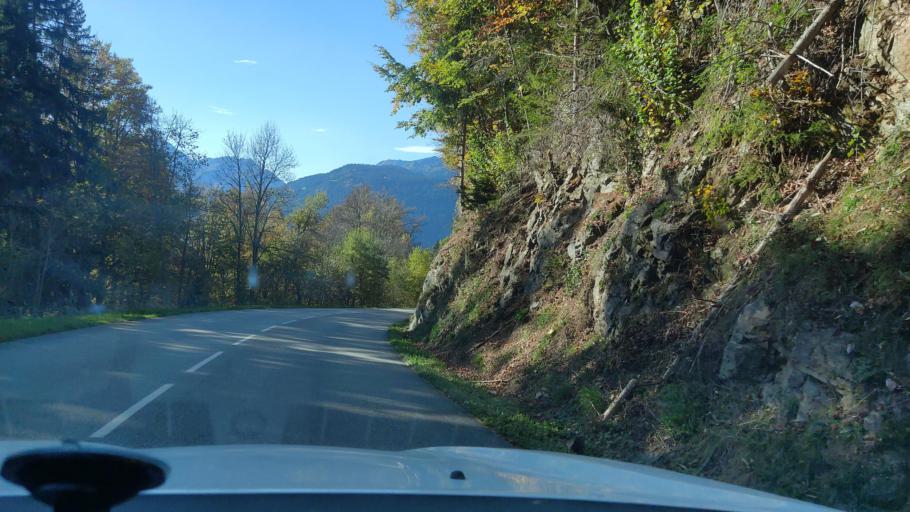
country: FR
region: Rhone-Alpes
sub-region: Departement de la Savoie
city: Beaufort
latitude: 45.7413
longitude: 6.5701
